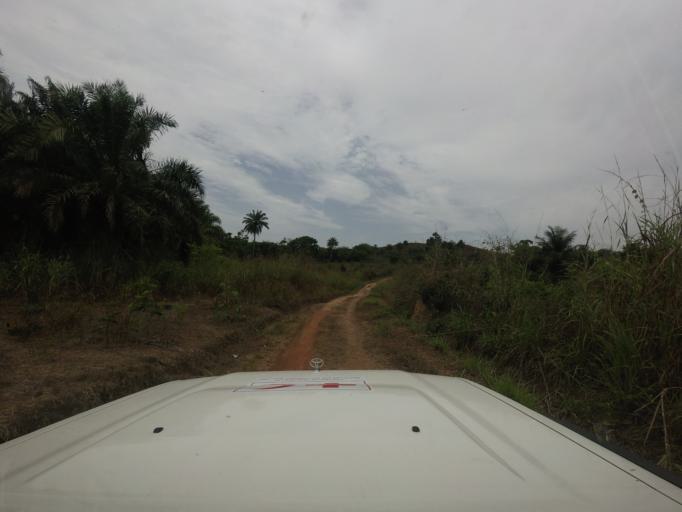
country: SL
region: Eastern Province
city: Buedu
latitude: 8.2621
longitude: -10.2880
